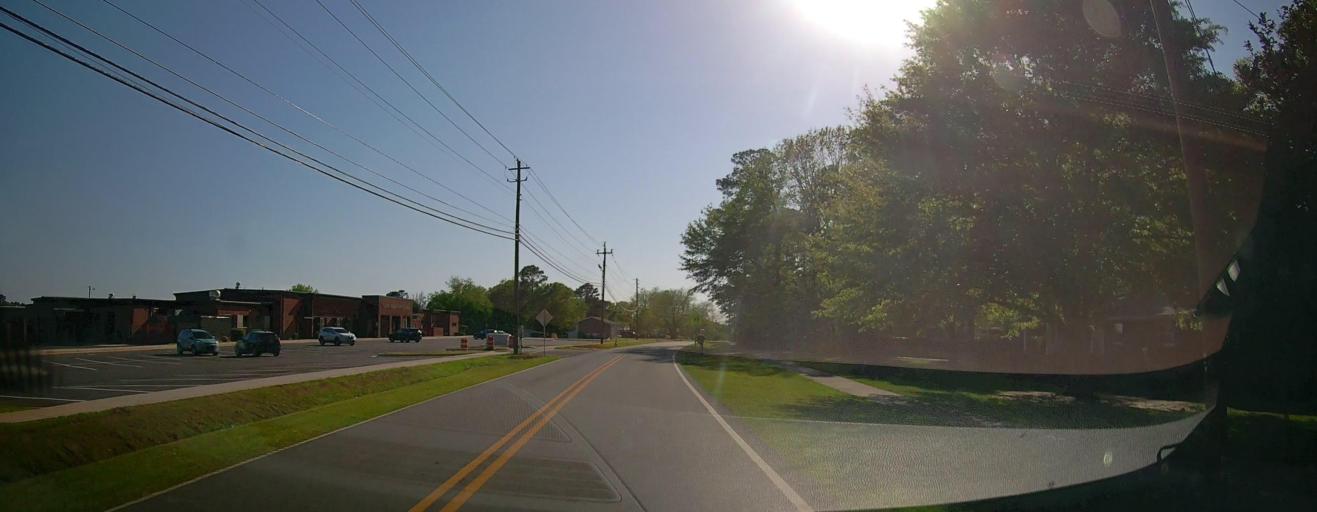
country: US
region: Georgia
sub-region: Houston County
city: Perry
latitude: 32.4505
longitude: -83.7210
